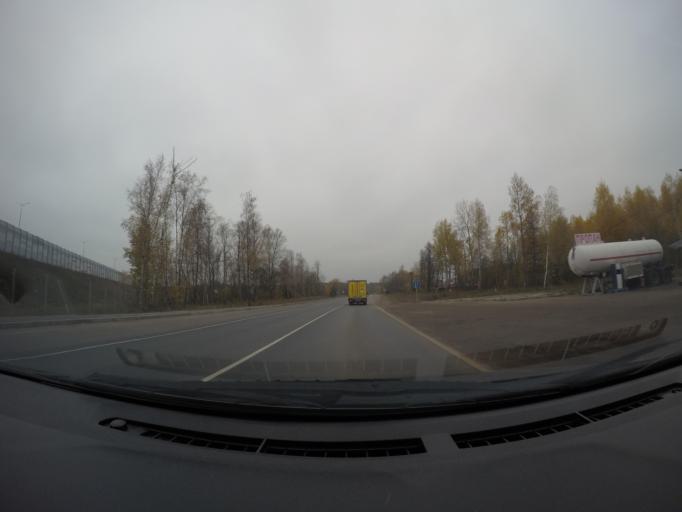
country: RU
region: Moskovskaya
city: Malyshevo
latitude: 55.5356
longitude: 38.4041
